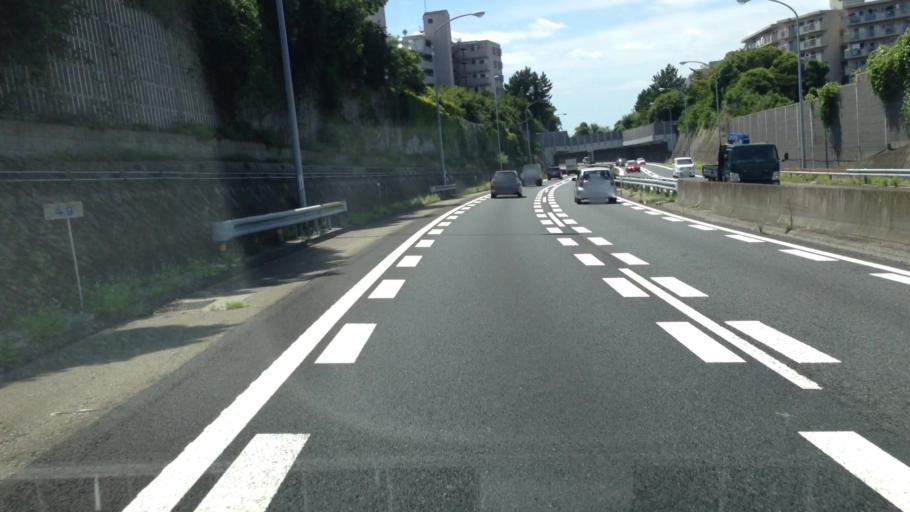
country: JP
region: Kanagawa
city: Yokohama
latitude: 35.4126
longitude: 139.5789
